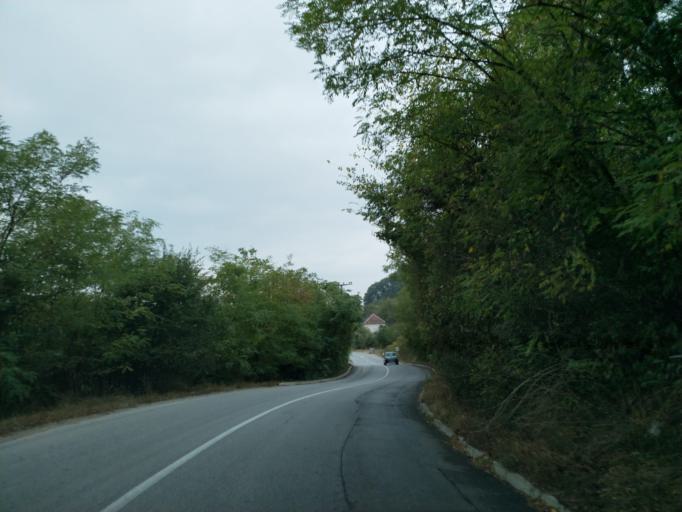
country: RS
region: Central Serbia
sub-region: Pomoravski Okrug
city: Jagodina
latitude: 44.0486
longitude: 21.1826
